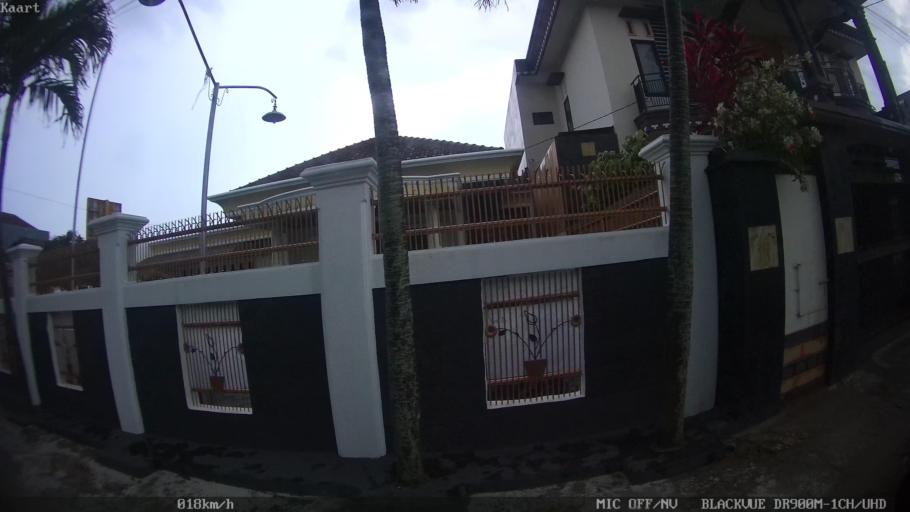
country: ID
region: Lampung
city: Kedaton
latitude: -5.3979
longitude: 105.2853
